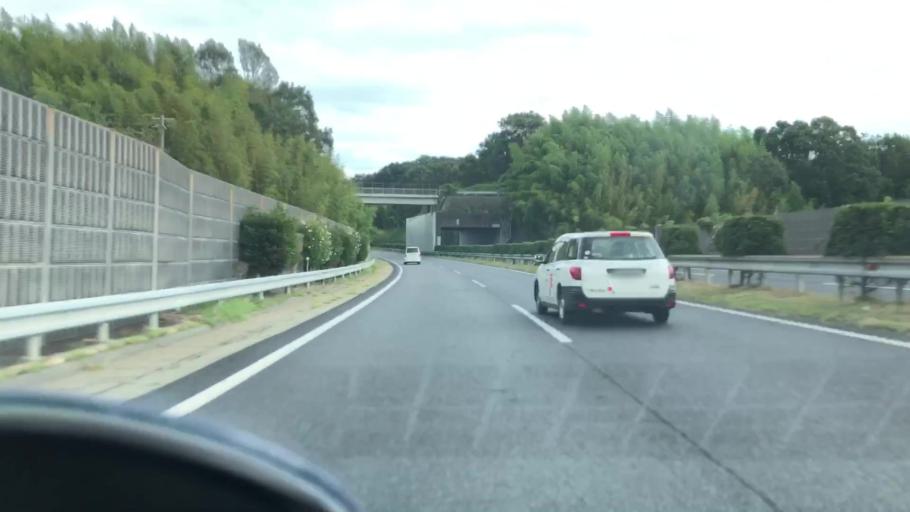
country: JP
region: Hyogo
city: Sandacho
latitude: 34.8867
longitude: 135.0985
